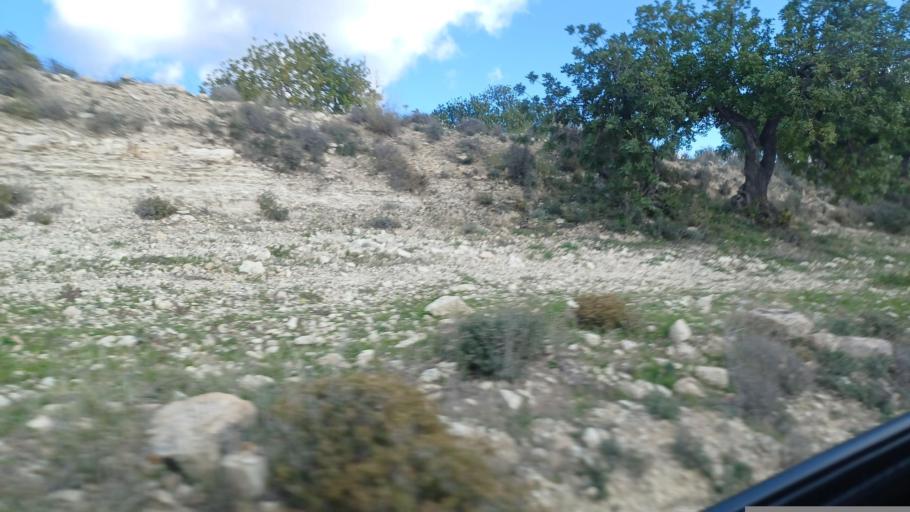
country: CY
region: Limassol
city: Pano Polemidia
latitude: 34.7733
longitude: 32.9764
